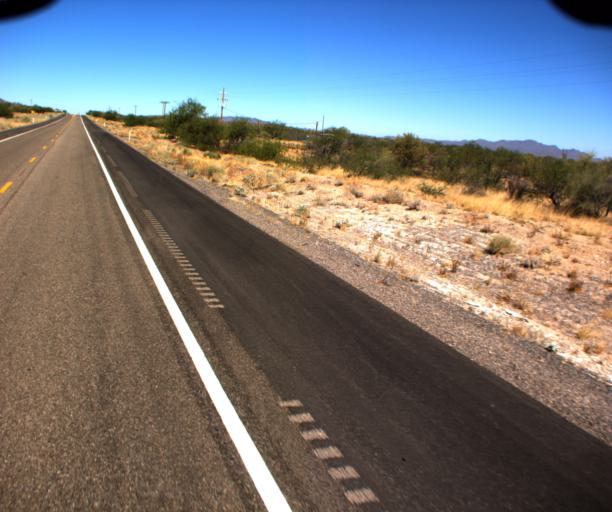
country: US
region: Arizona
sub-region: Pima County
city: Three Points
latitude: 32.0283
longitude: -111.5706
